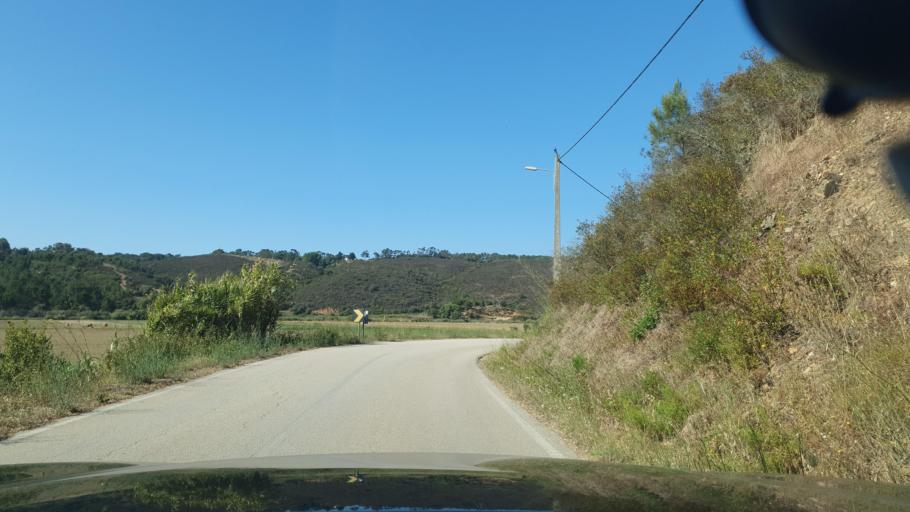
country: PT
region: Beja
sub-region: Odemira
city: Sao Teotonio
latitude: 37.4322
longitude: -8.7744
